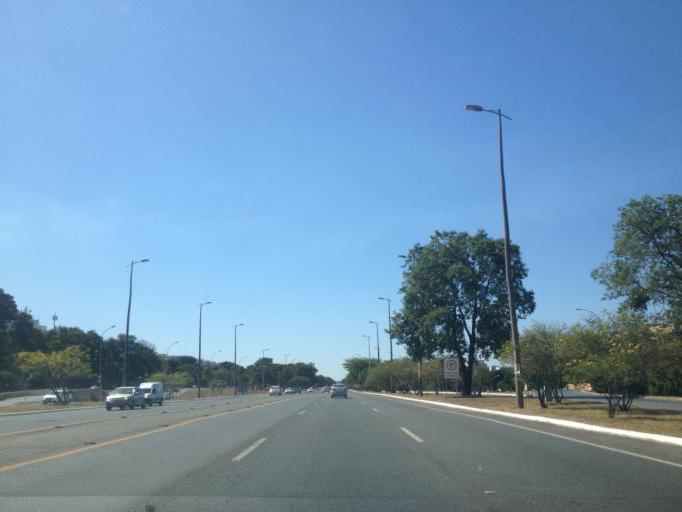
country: BR
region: Federal District
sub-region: Brasilia
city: Brasilia
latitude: -15.8353
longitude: -47.9260
